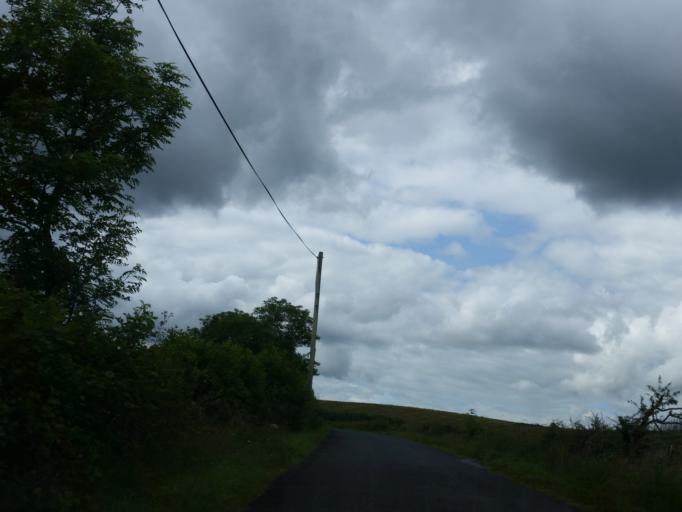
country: IE
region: Ulster
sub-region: County Monaghan
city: Clones
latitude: 54.2626
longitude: -7.2744
